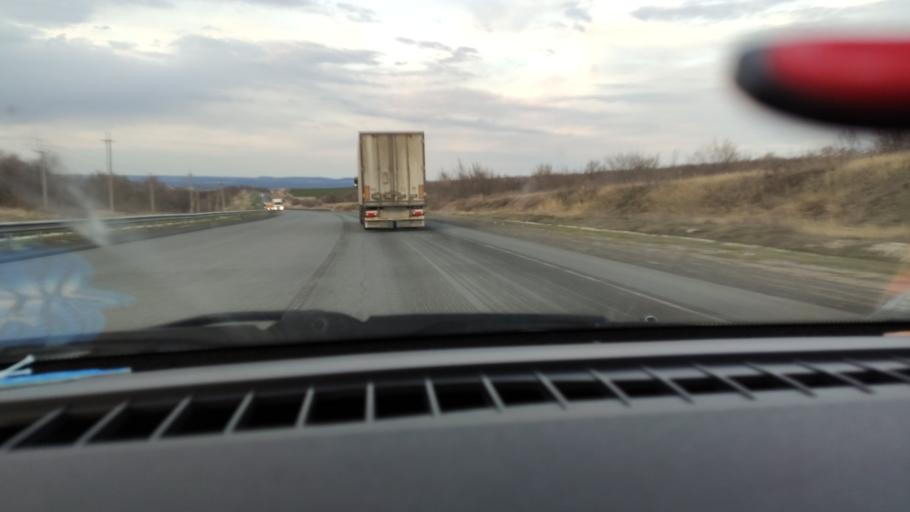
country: RU
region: Saratov
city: Shumeyka
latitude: 51.7814
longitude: 46.1266
